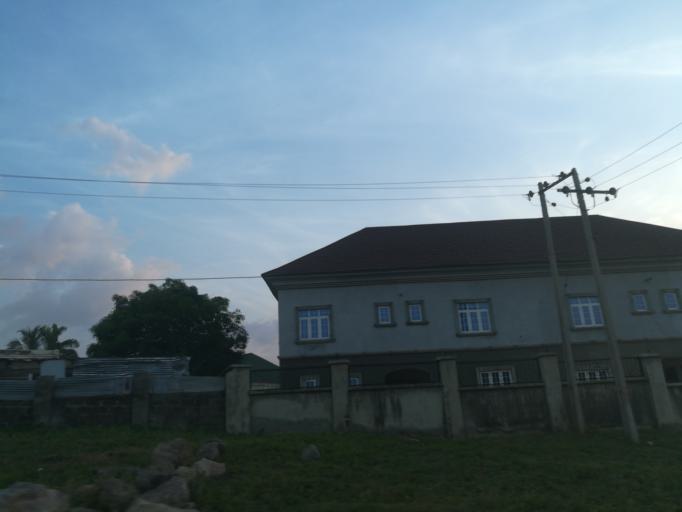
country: NG
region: Abuja Federal Capital Territory
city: Abuja
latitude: 9.0787
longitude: 7.3885
